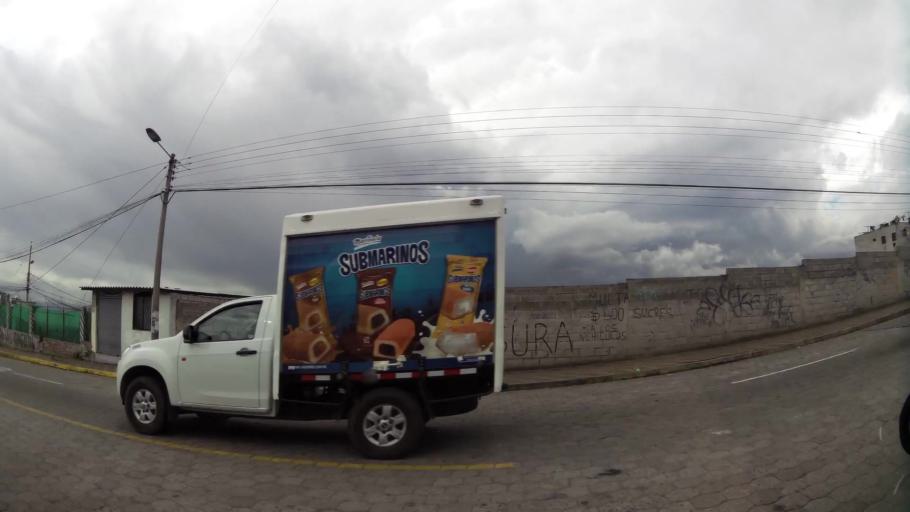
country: EC
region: Pichincha
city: Quito
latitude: -0.3250
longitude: -78.5534
